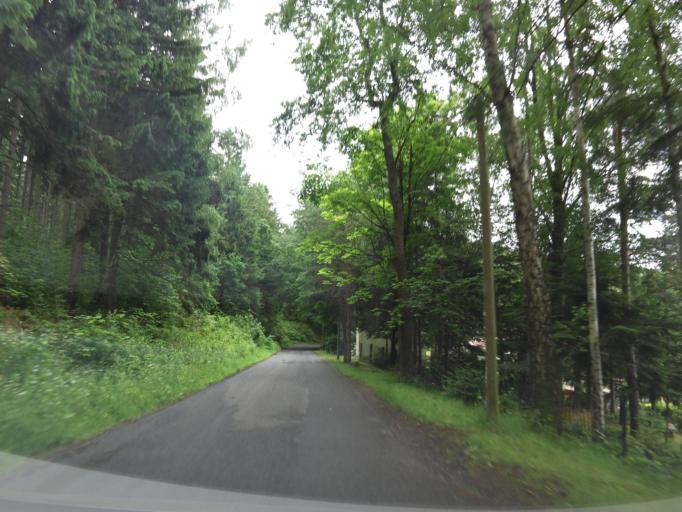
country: DE
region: Thuringia
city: Tabarz
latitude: 50.8809
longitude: 10.5255
